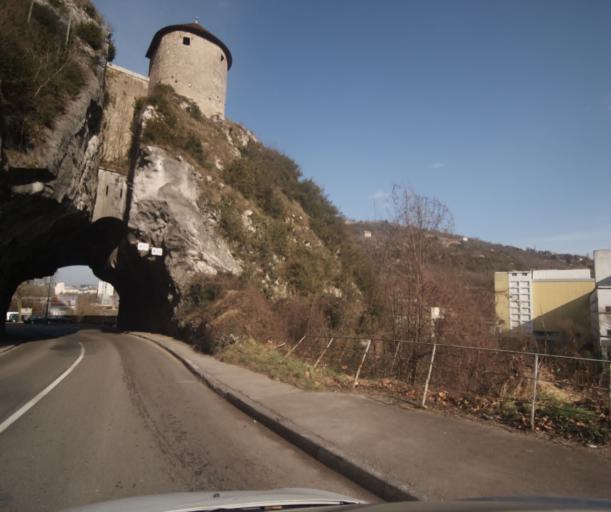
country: FR
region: Franche-Comte
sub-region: Departement du Doubs
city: Besancon
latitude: 47.2283
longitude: 6.0383
